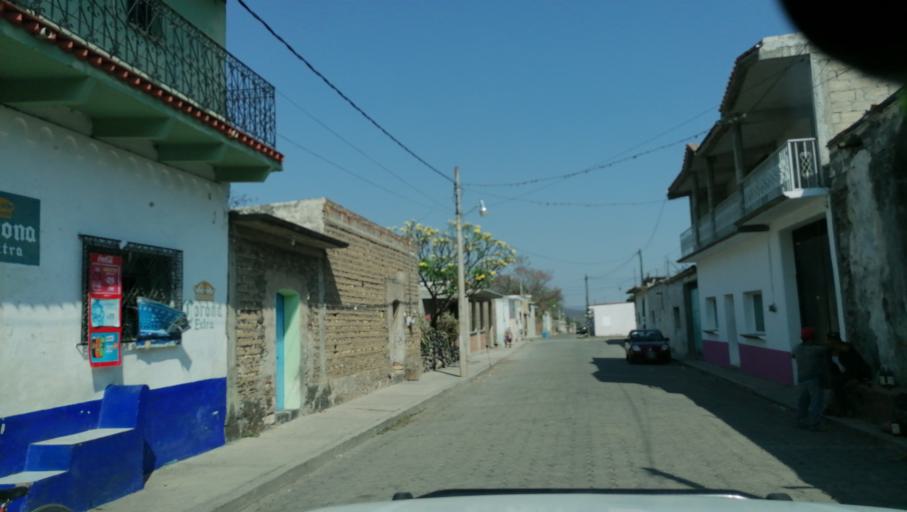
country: MX
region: Puebla
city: Huaquechula
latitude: 18.7727
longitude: -98.5446
